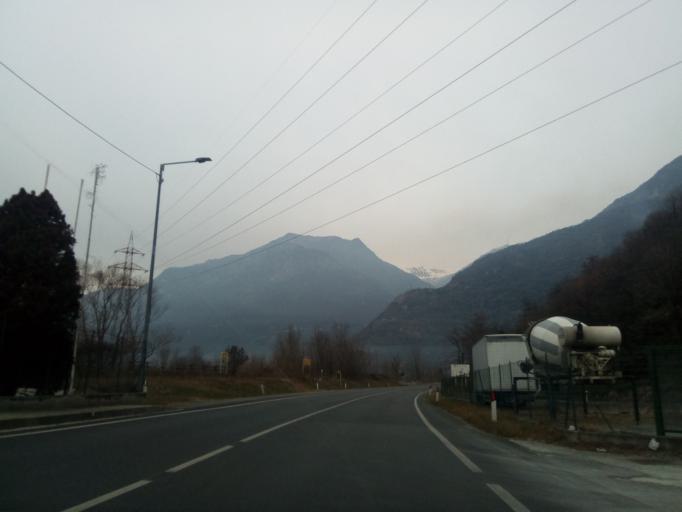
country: IT
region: Piedmont
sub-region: Provincia di Torino
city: Carema
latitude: 45.5732
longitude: 7.8102
